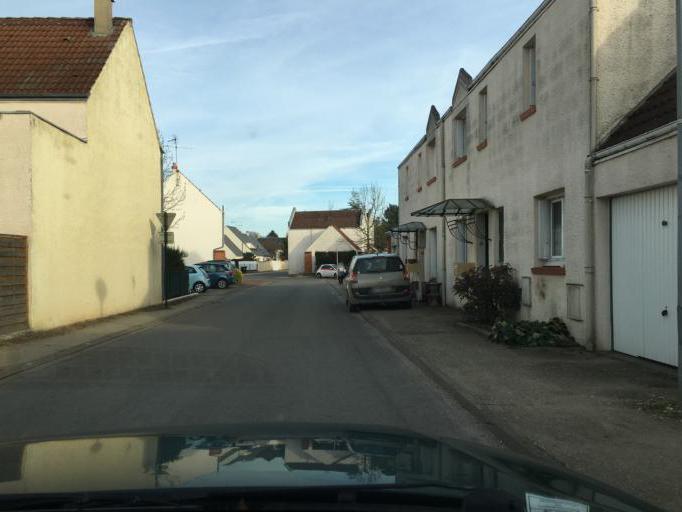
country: FR
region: Centre
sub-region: Departement du Loiret
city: La Ferte-Saint-Aubin
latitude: 47.7171
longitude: 1.9389
